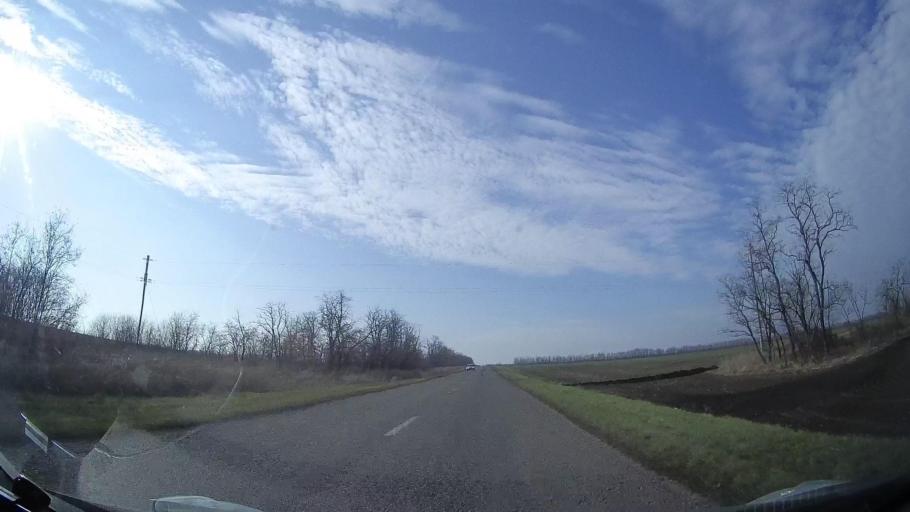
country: RU
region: Rostov
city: Gigant
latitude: 46.8471
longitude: 41.3008
